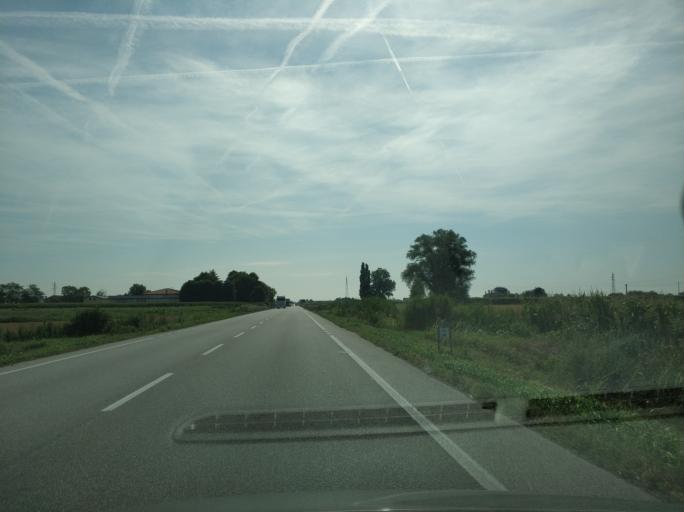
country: IT
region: Veneto
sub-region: Provincia di Padova
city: Arre
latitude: 45.2116
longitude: 11.9492
